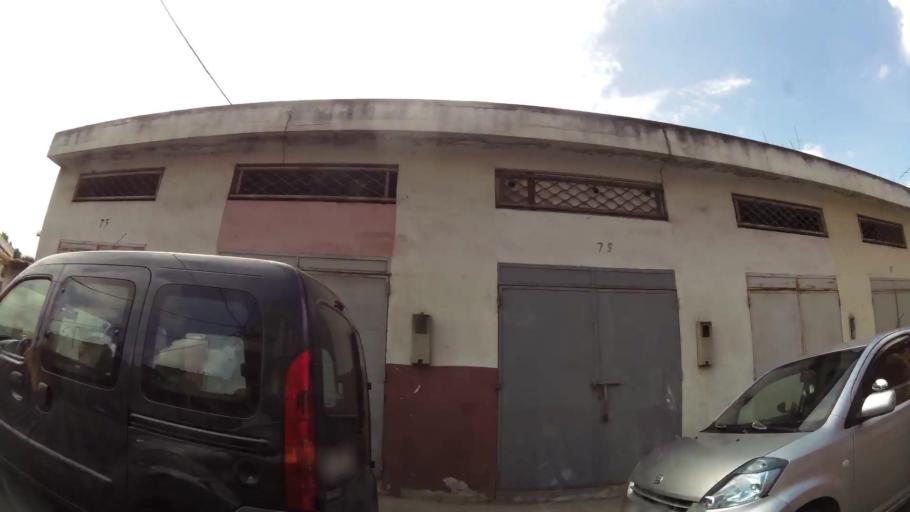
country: MA
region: Gharb-Chrarda-Beni Hssen
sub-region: Kenitra Province
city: Kenitra
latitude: 34.2655
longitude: -6.5738
